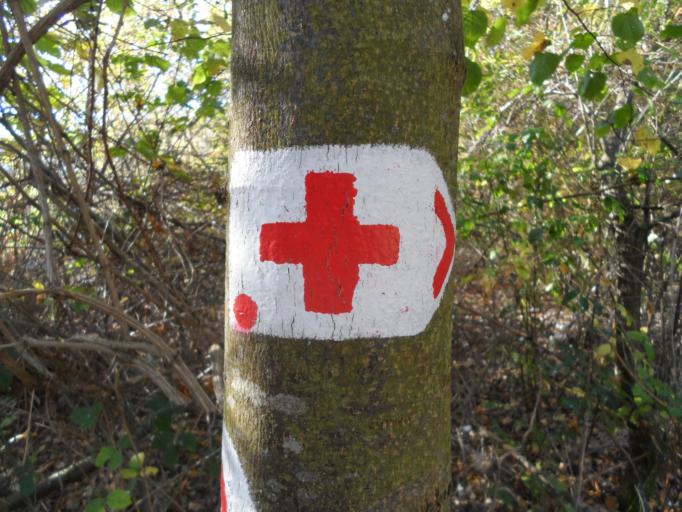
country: HU
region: Veszprem
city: Herend
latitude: 47.2341
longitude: 17.6752
